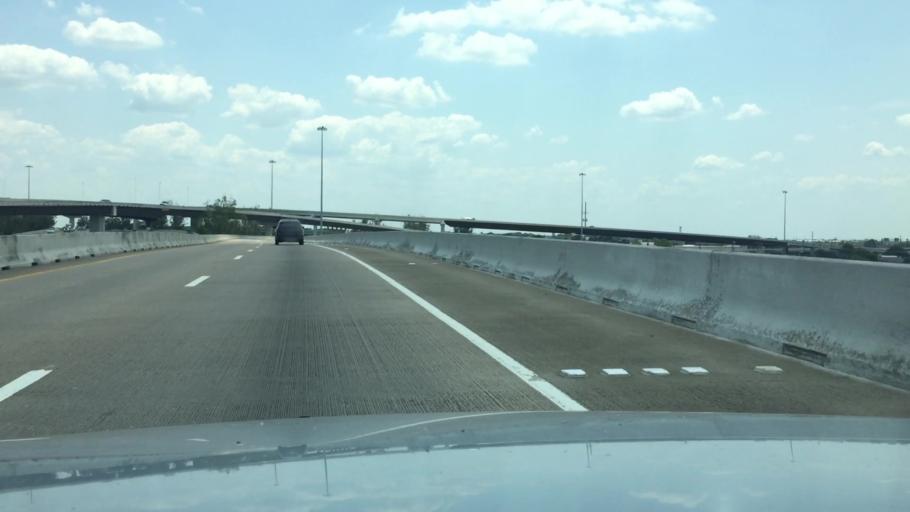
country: US
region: Texas
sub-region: Fort Bend County
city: Meadows Place
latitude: 29.6641
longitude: -95.5598
